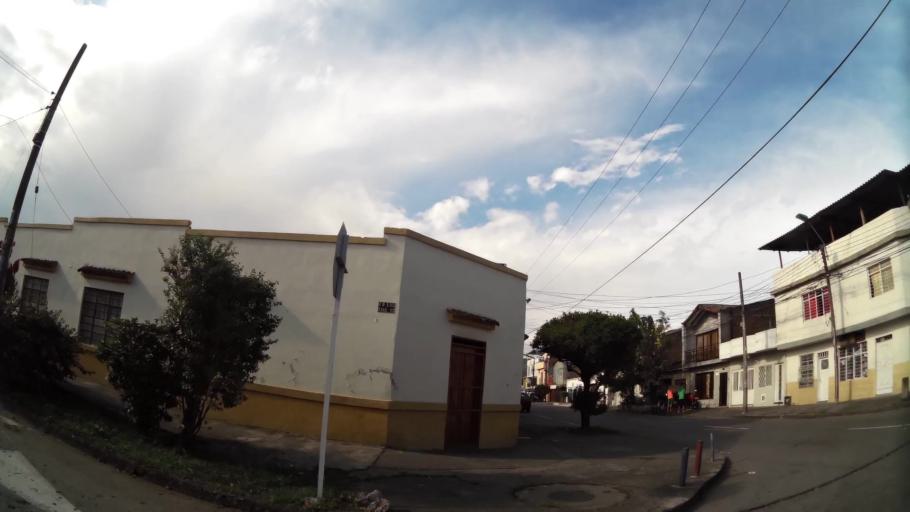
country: CO
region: Valle del Cauca
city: Cali
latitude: 3.4217
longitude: -76.5243
